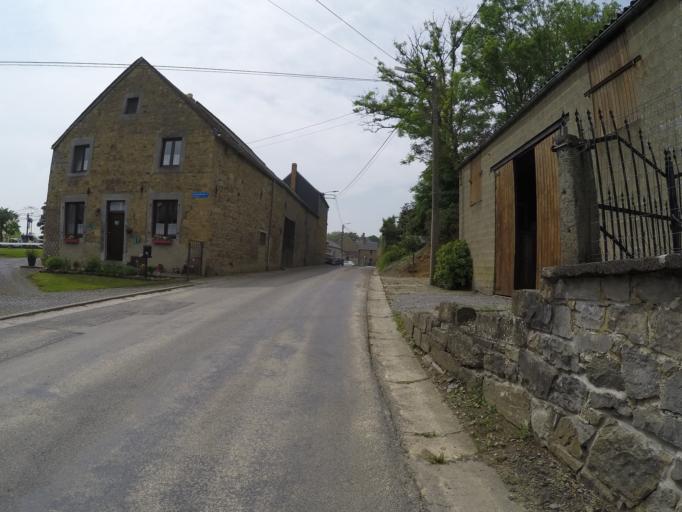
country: BE
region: Wallonia
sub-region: Province de Namur
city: Assesse
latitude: 50.3350
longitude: 4.9920
